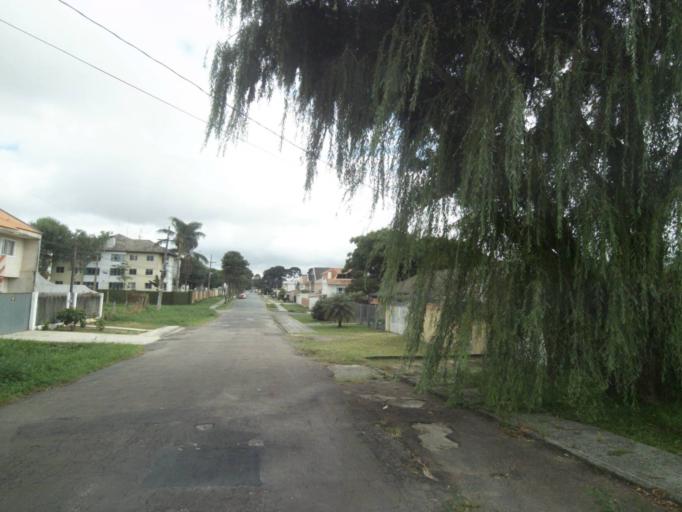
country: BR
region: Parana
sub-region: Pinhais
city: Pinhais
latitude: -25.4584
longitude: -49.2201
